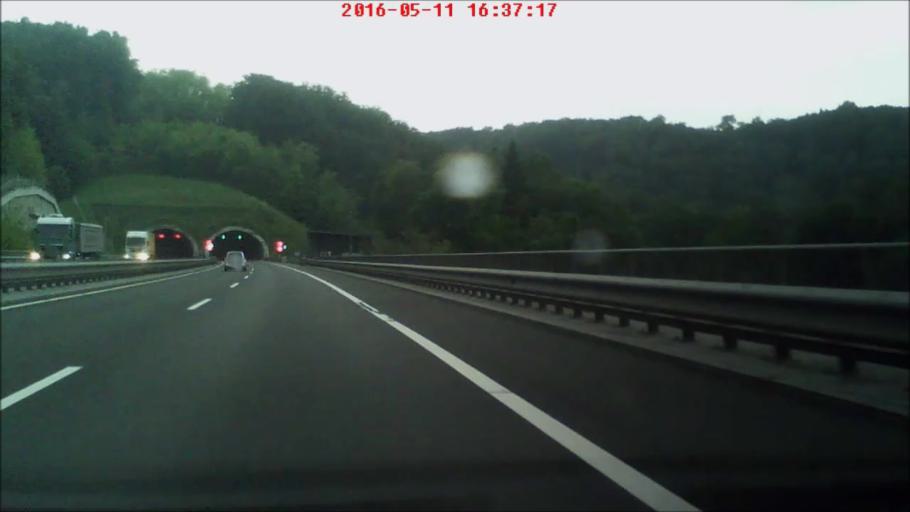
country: SI
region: Pesnica
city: Pesnica pri Mariboru
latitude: 46.5704
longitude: 15.6869
